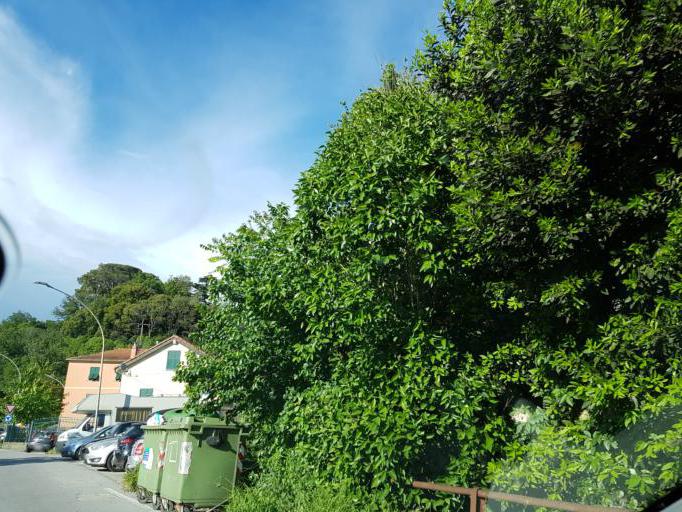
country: IT
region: Liguria
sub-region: Provincia di Genova
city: Manesseno
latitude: 44.4821
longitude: 8.9219
